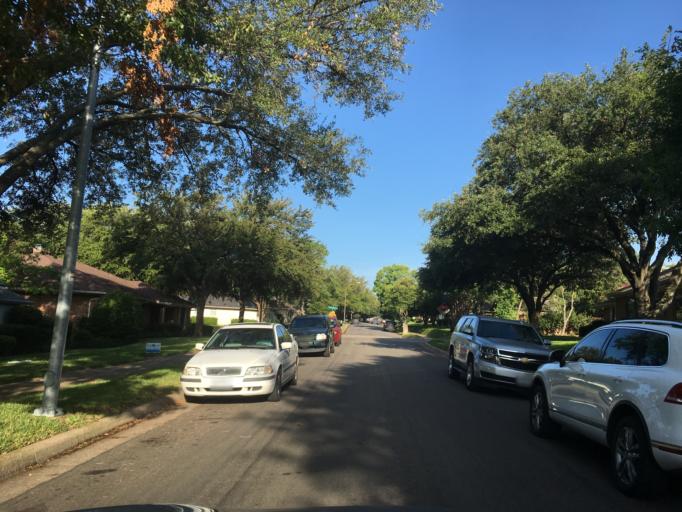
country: US
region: Texas
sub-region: Dallas County
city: Richardson
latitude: 32.8884
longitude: -96.7360
